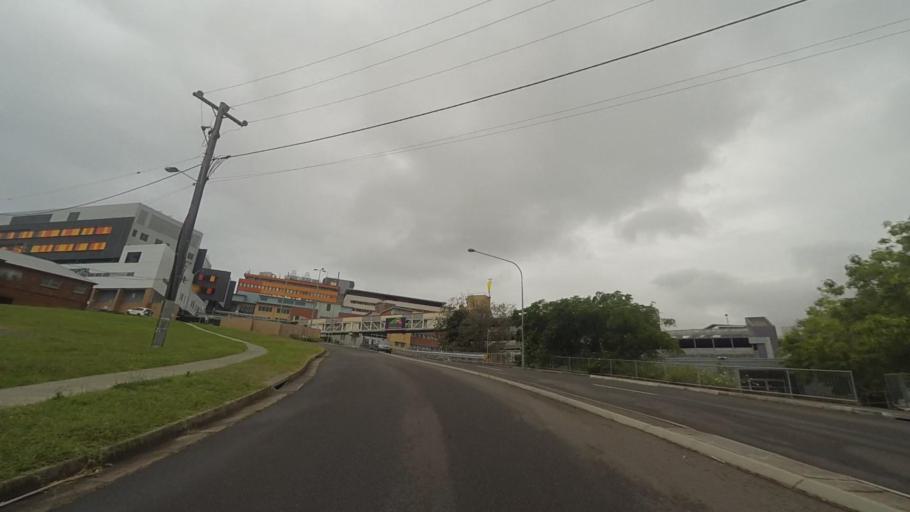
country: AU
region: New South Wales
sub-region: Wollongong
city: Gwynneville
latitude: -34.4233
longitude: 150.8824
